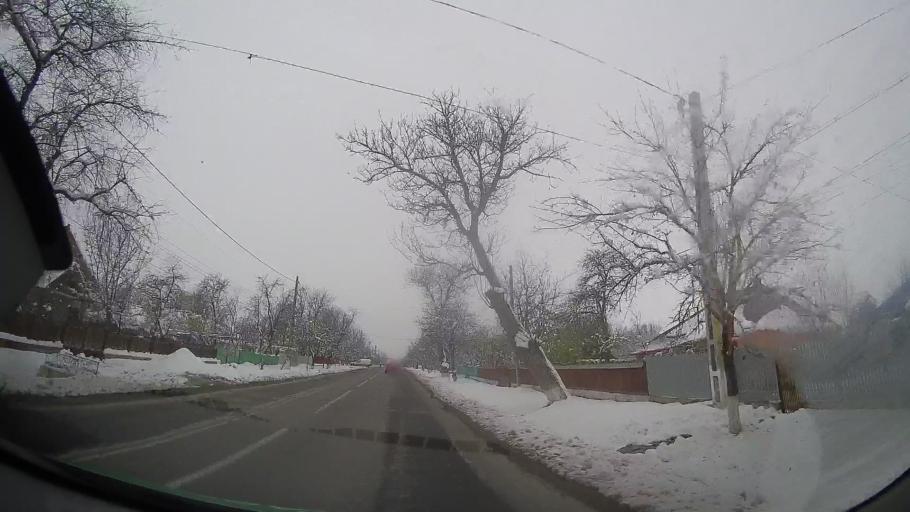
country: RO
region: Vaslui
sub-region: Comuna Negresti
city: Negresti
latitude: 46.8391
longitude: 27.4124
